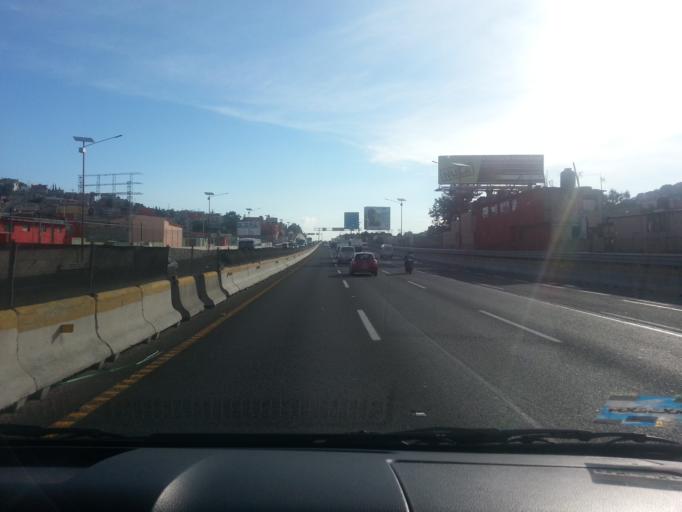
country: MX
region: Mexico
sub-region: Tlalnepantla de Baz
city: Puerto Escondido (Tepeolulco Puerto Escondido)
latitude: 19.5495
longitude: -99.0689
